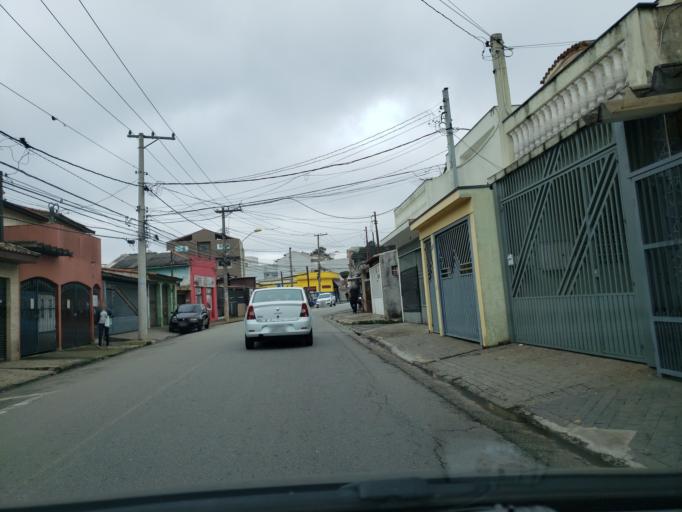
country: BR
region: Sao Paulo
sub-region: Santo Andre
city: Santo Andre
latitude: -23.6416
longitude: -46.5315
